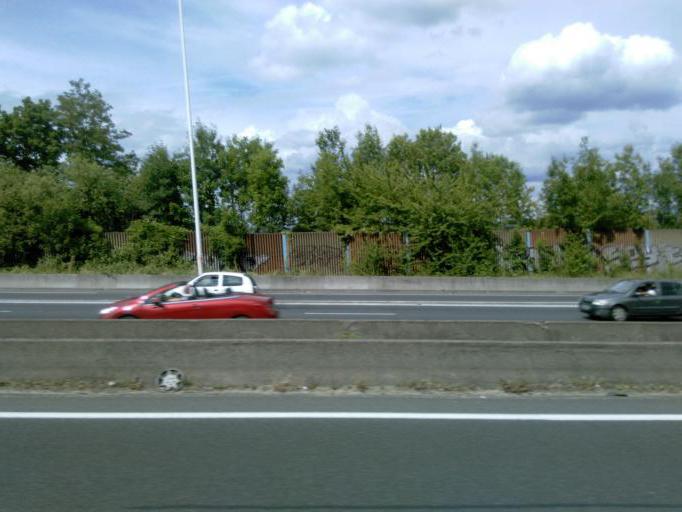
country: FR
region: Ile-de-France
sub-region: Departement du Val-d'Oise
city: Franconville
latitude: 48.9771
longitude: 2.2336
